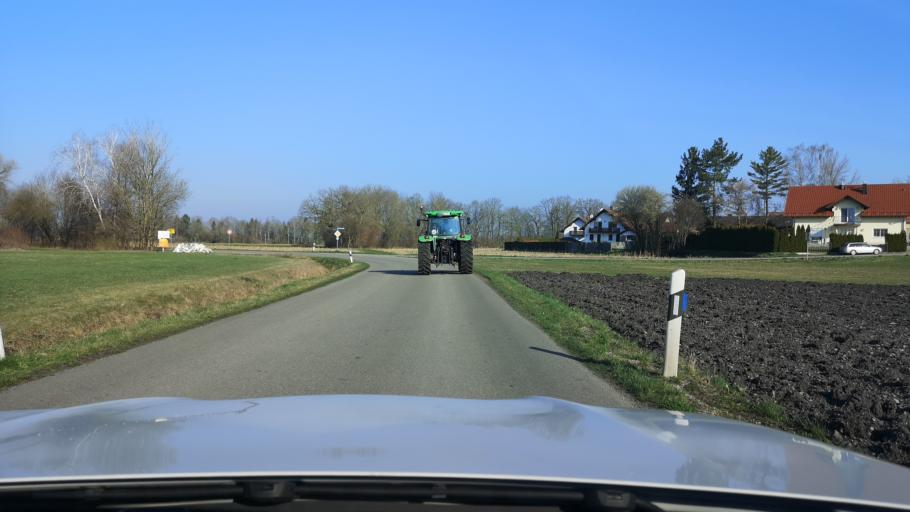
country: DE
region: Bavaria
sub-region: Upper Bavaria
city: Eichenried
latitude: 48.2449
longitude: 11.7765
